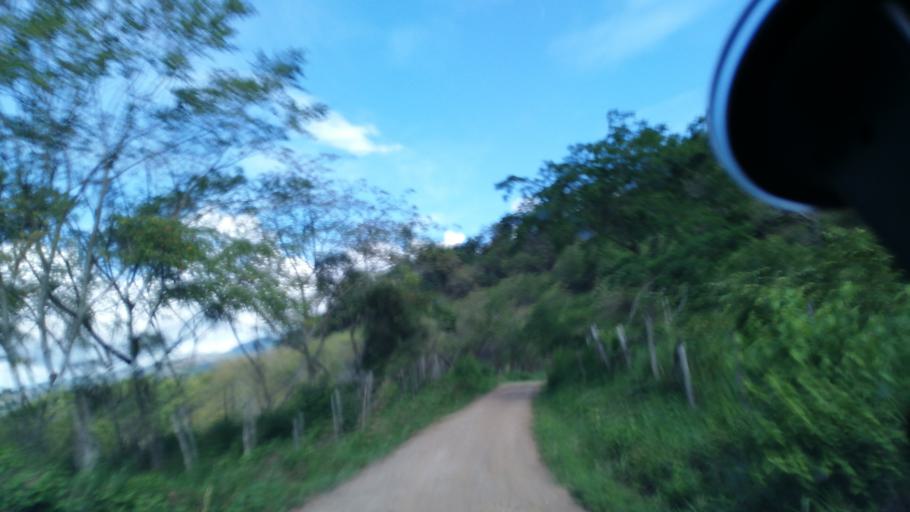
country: CO
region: Cundinamarca
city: Quipile
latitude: 4.7624
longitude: -74.6205
